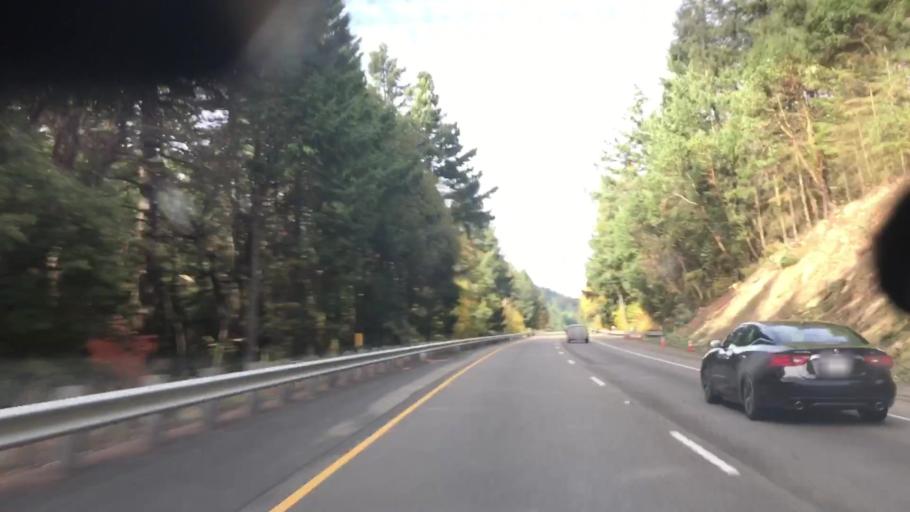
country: US
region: Oregon
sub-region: Douglas County
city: Canyonville
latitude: 42.8184
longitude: -123.2613
